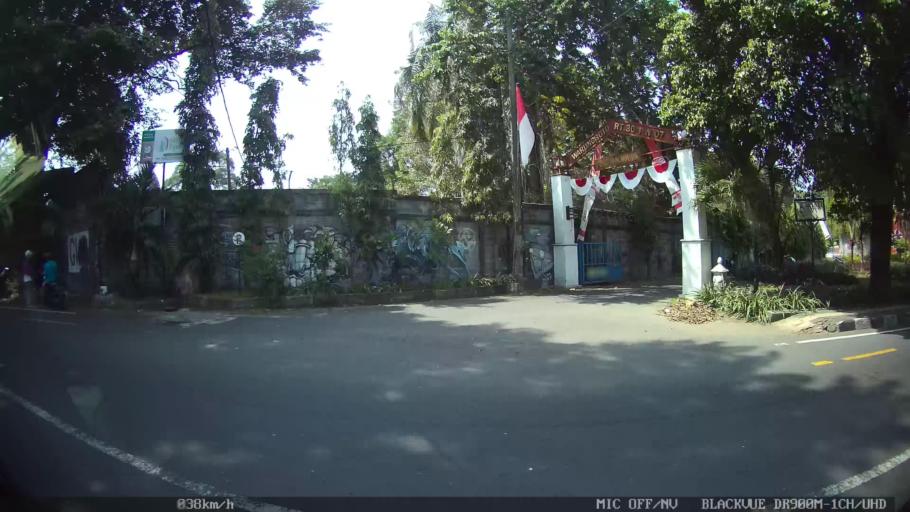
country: ID
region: Daerah Istimewa Yogyakarta
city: Yogyakarta
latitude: -7.8078
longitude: 110.3943
